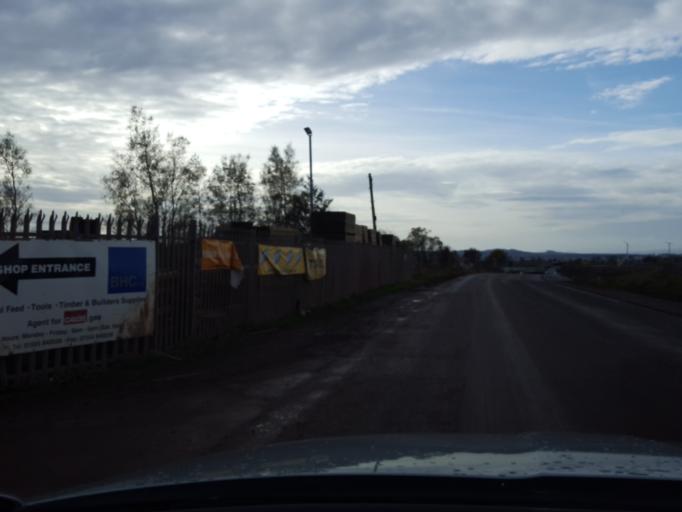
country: GB
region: Scotland
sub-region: South Lanarkshire
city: Carnwath
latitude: 55.7039
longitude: -3.6178
